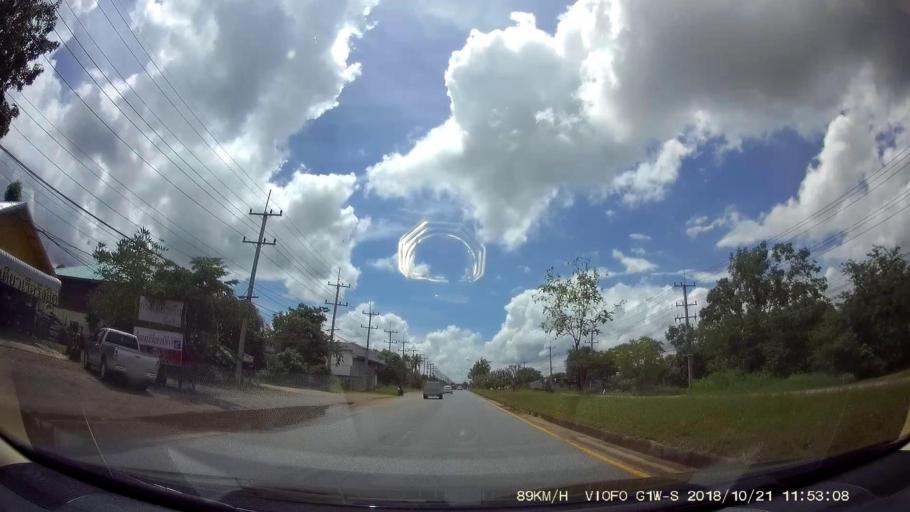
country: TH
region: Chaiyaphum
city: Chatturat
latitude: 15.5998
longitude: 101.9077
